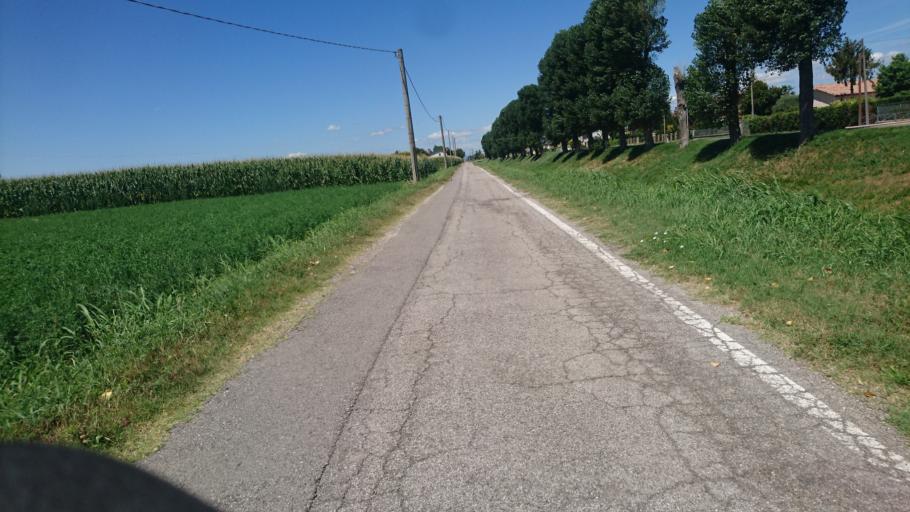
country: IT
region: Veneto
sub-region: Provincia di Padova
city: Sant'Angelo di Piove di Sacco
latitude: 45.3047
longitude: 12.0056
